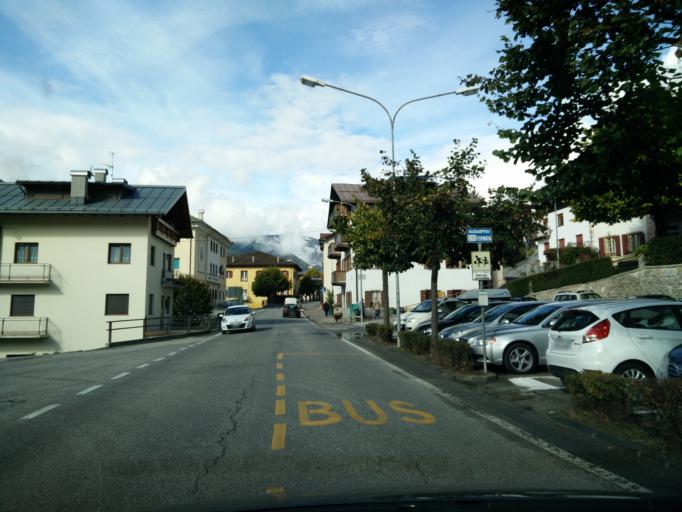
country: IT
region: Veneto
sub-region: Provincia di Belluno
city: Auronzo
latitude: 46.5453
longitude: 12.4577
